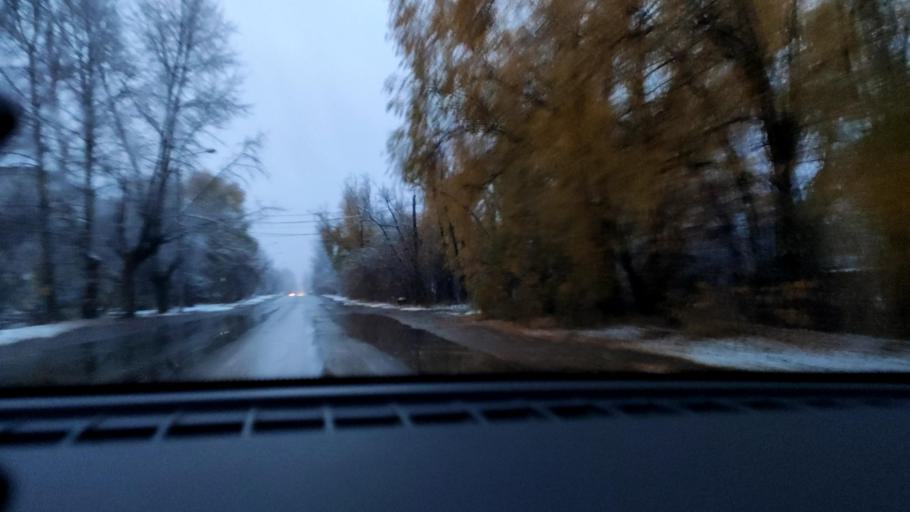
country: RU
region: Perm
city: Overyata
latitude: 58.0122
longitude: 55.9533
